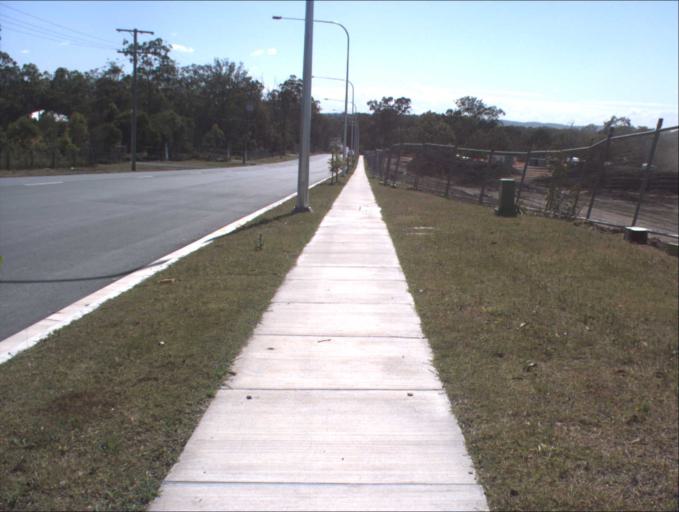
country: AU
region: Queensland
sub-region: Logan
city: Woodridge
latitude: -27.6551
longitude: 153.0809
